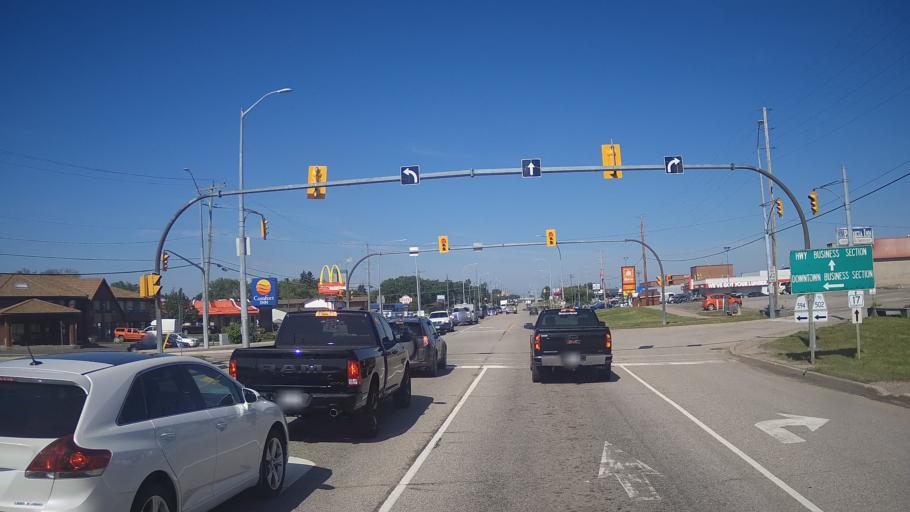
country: CA
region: Ontario
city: Dryden
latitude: 49.7863
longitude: -92.8207
